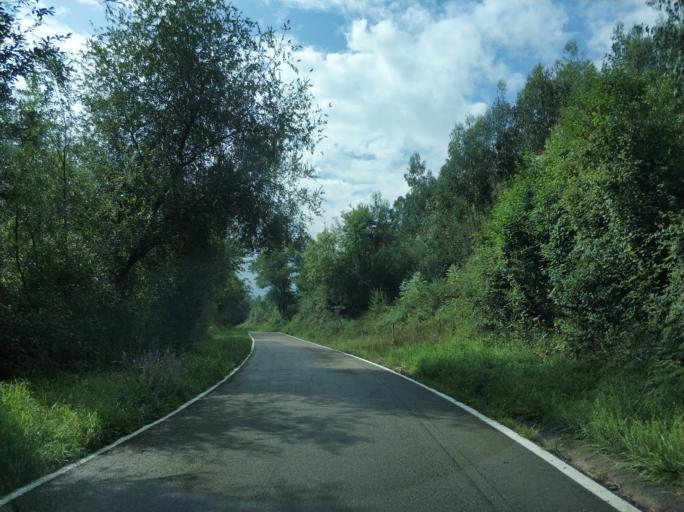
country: ES
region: Cantabria
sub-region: Provincia de Cantabria
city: Polanco
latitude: 43.3780
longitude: -3.9719
